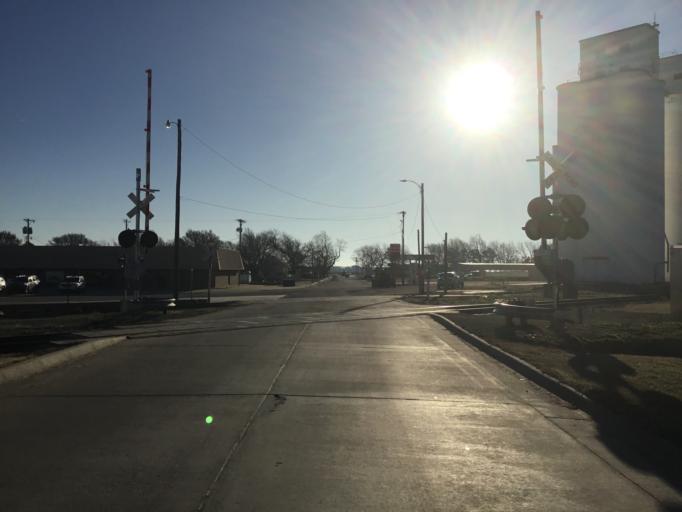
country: US
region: Kansas
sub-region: Sedgwick County
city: Saint Marys
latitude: 37.7891
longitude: -97.6307
